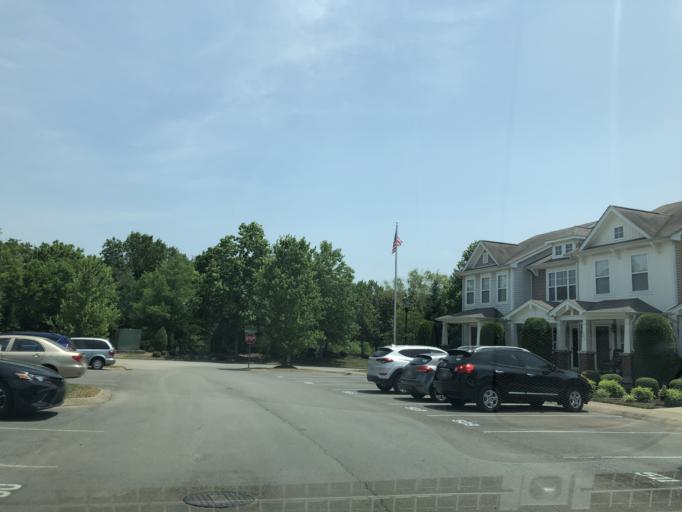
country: US
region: Tennessee
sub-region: Rutherford County
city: La Vergne
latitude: 36.0523
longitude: -86.6125
